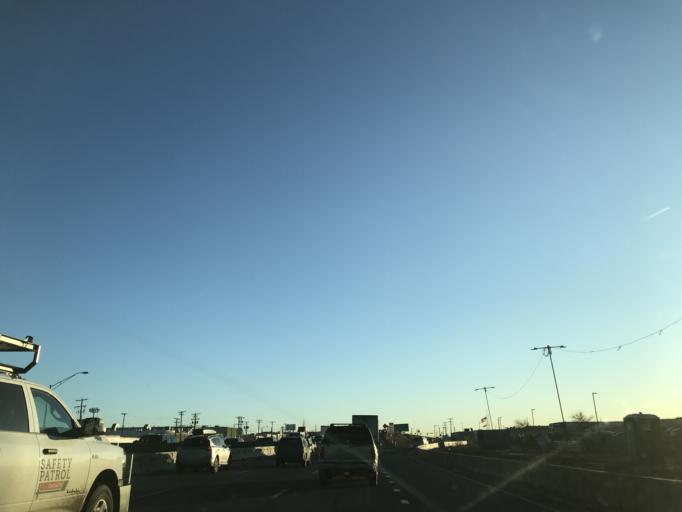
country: US
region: Colorado
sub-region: Adams County
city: Commerce City
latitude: 39.7800
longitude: -104.9371
